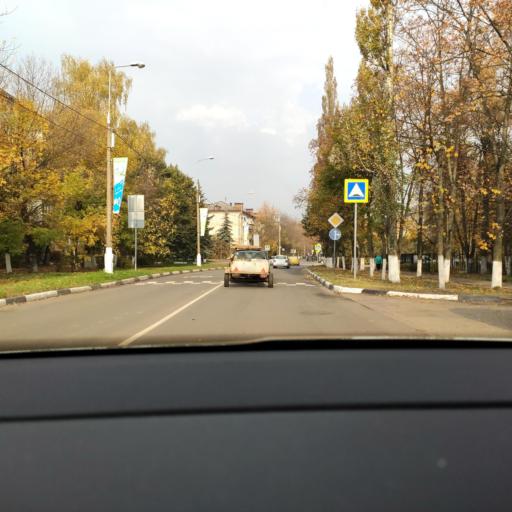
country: RU
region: Moskovskaya
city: Ivanteyevka
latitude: 55.9710
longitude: 37.9053
